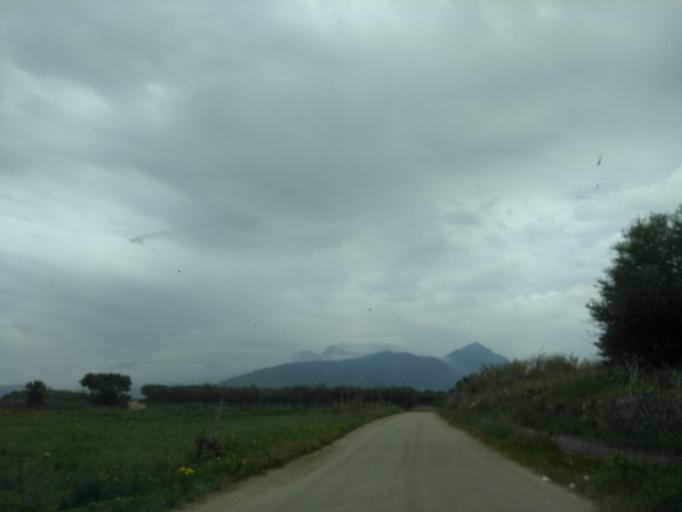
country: IT
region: Sicily
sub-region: Palermo
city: Partinico
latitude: 37.9945
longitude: 13.0776
